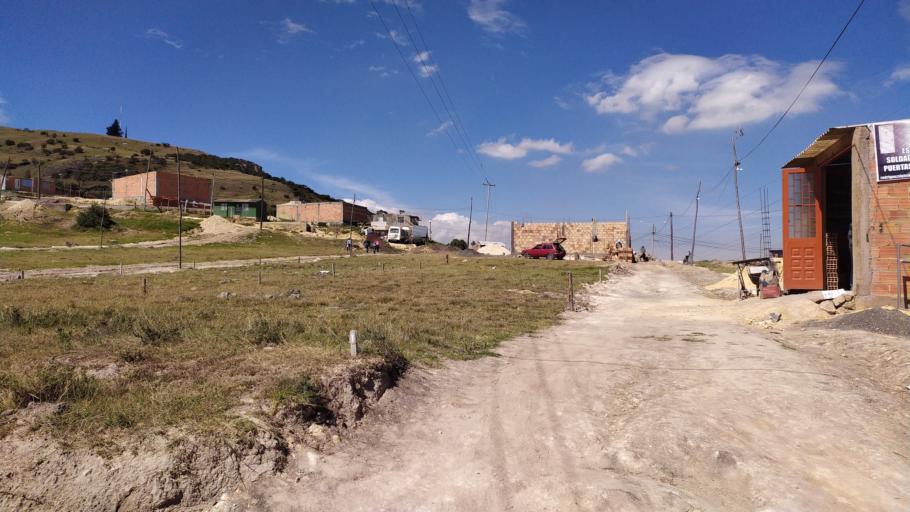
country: CO
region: Cundinamarca
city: Soacha
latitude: 4.5406
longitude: -74.1713
